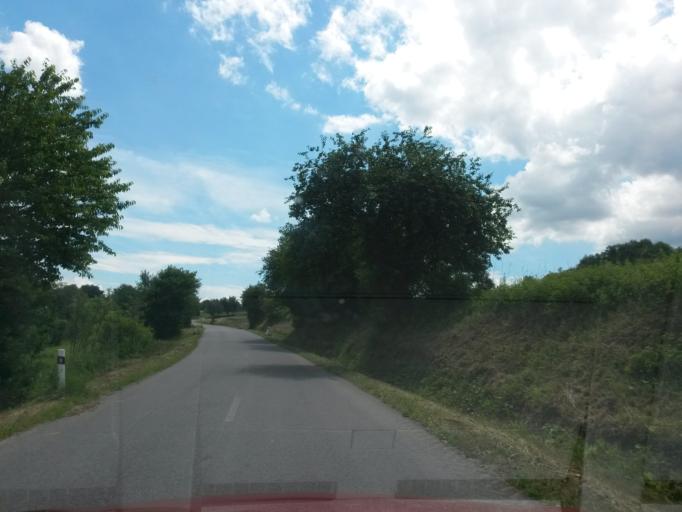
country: SK
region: Presovsky
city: Sabinov
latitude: 48.9601
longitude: 21.0862
